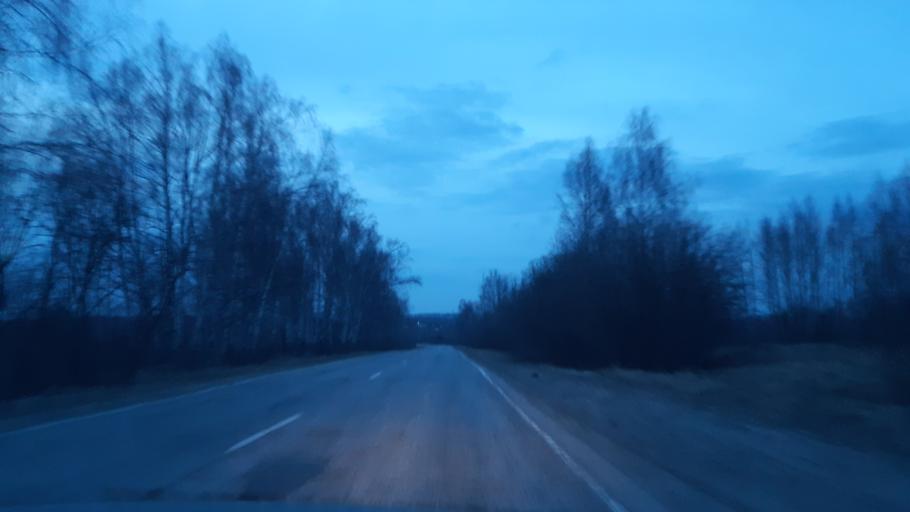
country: RU
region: Vladimir
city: Luknovo
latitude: 56.2057
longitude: 42.0330
